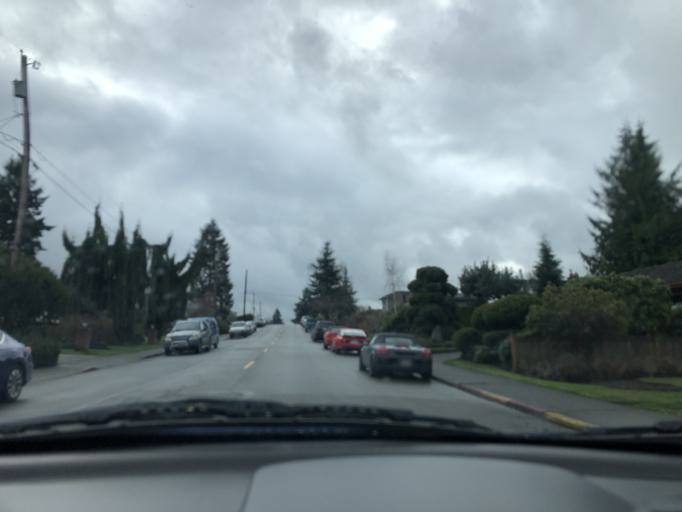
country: US
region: Washington
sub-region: Snohomish County
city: Everett
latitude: 48.0095
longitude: -122.2065
